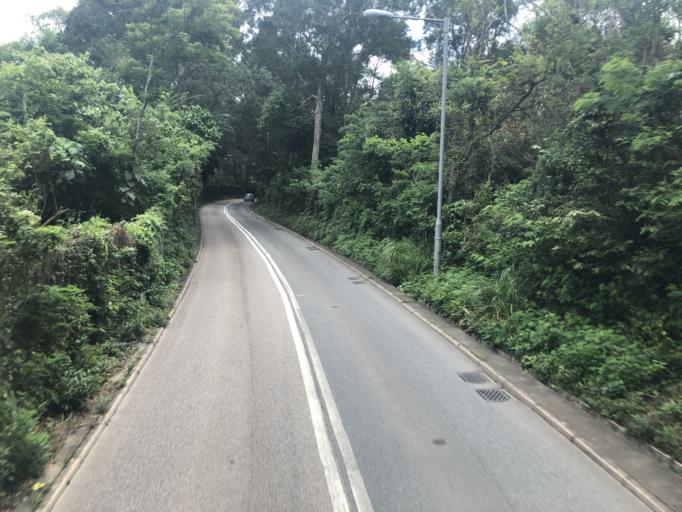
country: HK
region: Tai Po
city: Tai Po
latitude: 22.4883
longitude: 114.1165
